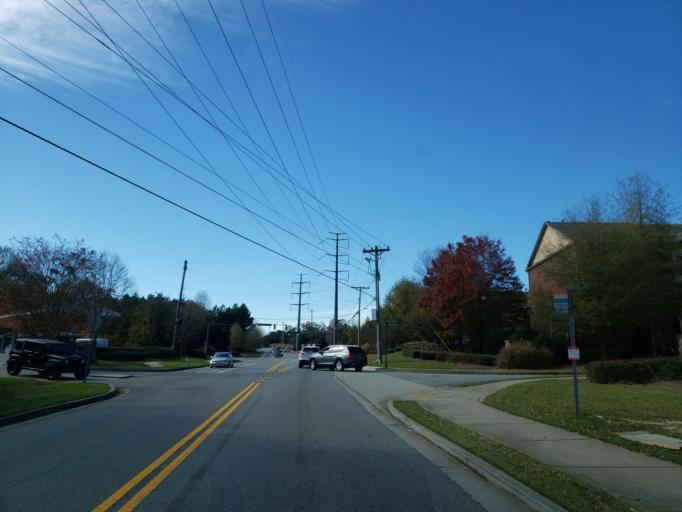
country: US
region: Georgia
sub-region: Fulton County
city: Alpharetta
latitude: 34.0979
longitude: -84.2630
